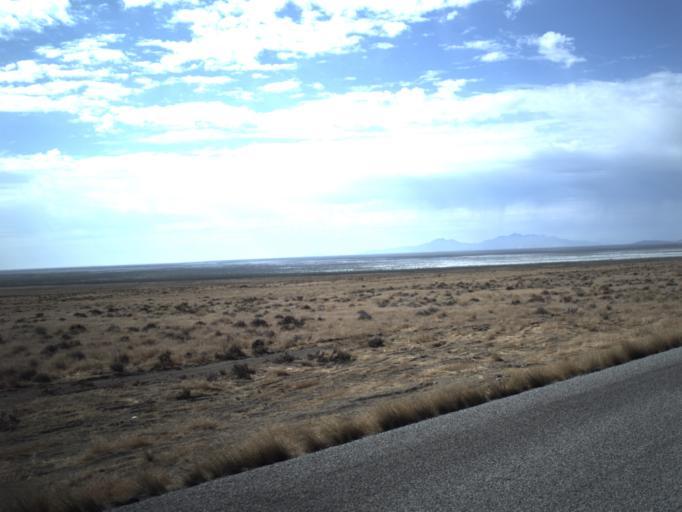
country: US
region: Utah
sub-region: Tooele County
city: Wendover
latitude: 41.4804
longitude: -113.6301
